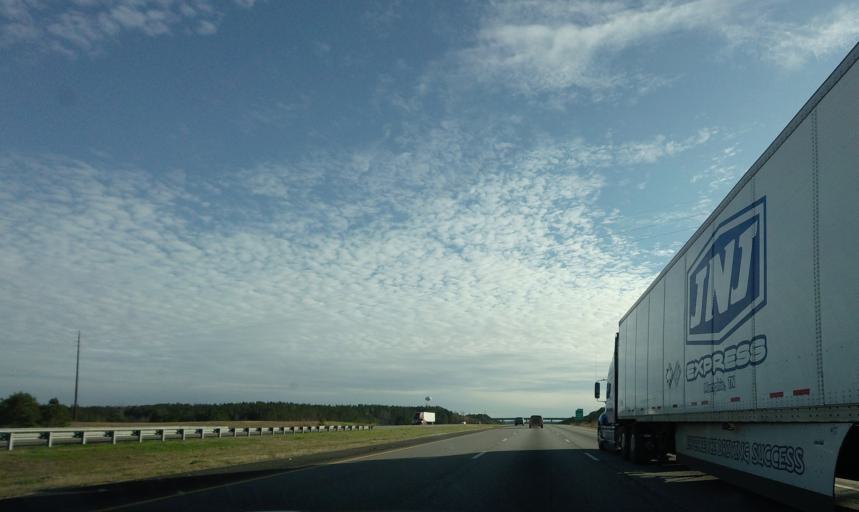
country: US
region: Alabama
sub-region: Walker County
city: Cordova
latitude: 33.7562
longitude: -87.2052
